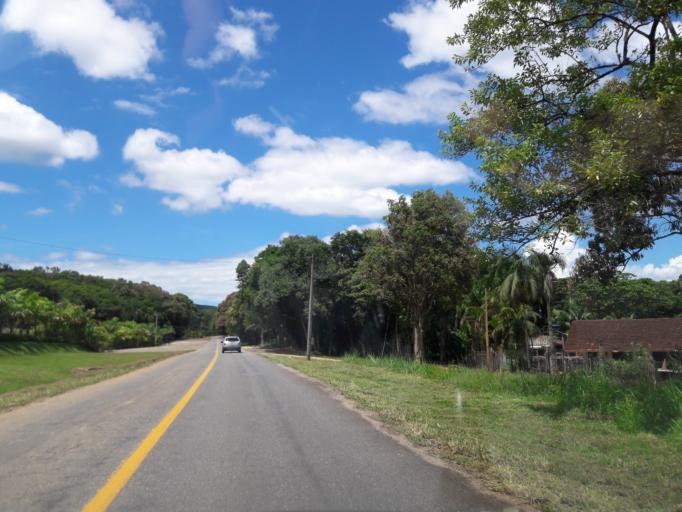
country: BR
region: Parana
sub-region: Antonina
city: Antonina
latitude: -25.4153
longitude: -48.8339
